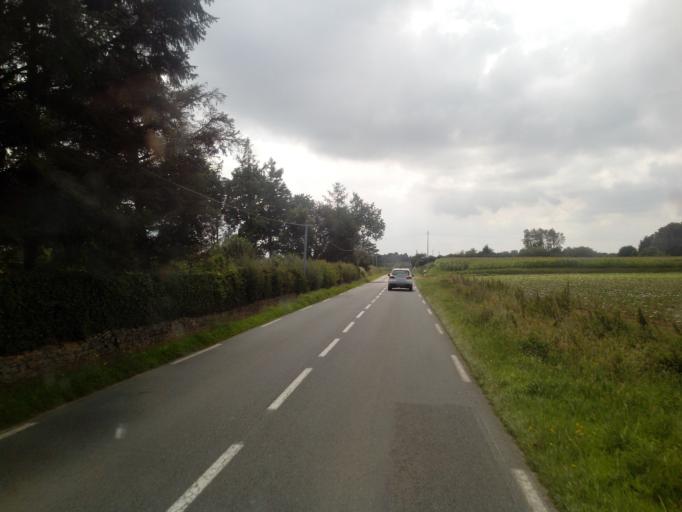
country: FR
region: Brittany
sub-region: Departement des Cotes-d'Armor
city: Plouezec
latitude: 48.7371
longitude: -2.9812
